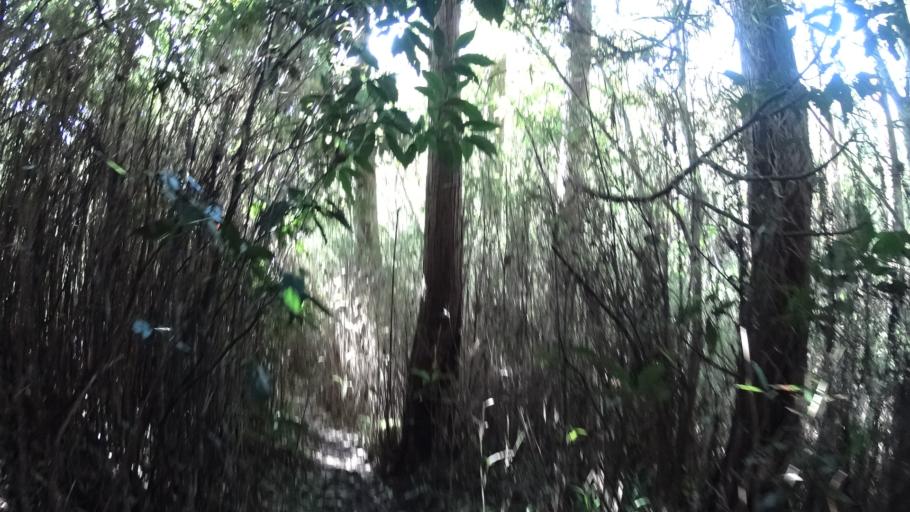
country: JP
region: Kanagawa
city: Zushi
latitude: 35.2922
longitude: 139.6222
